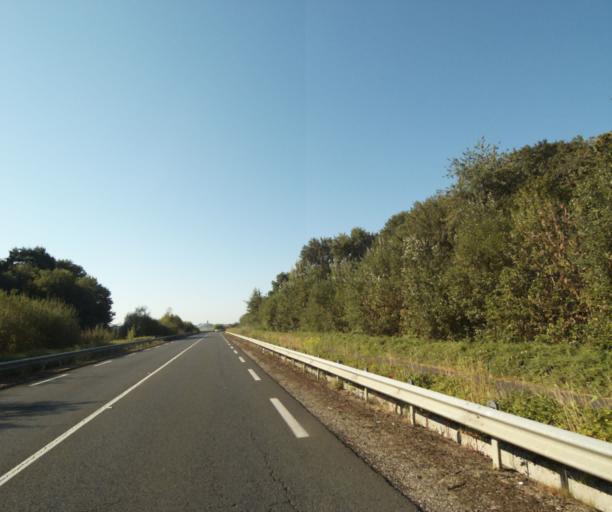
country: FR
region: Ile-de-France
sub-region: Departement de Seine-et-Marne
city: Savigny-le-Temple
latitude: 48.5946
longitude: 2.6049
